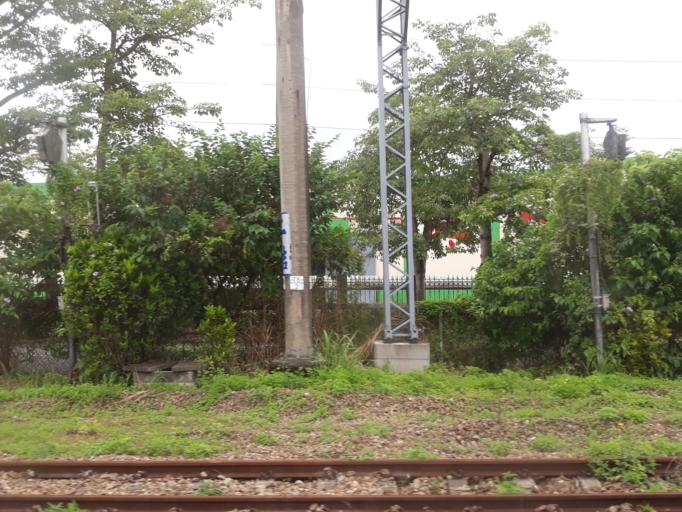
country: TW
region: Taiwan
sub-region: Yilan
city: Yilan
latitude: 24.6969
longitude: 121.7752
